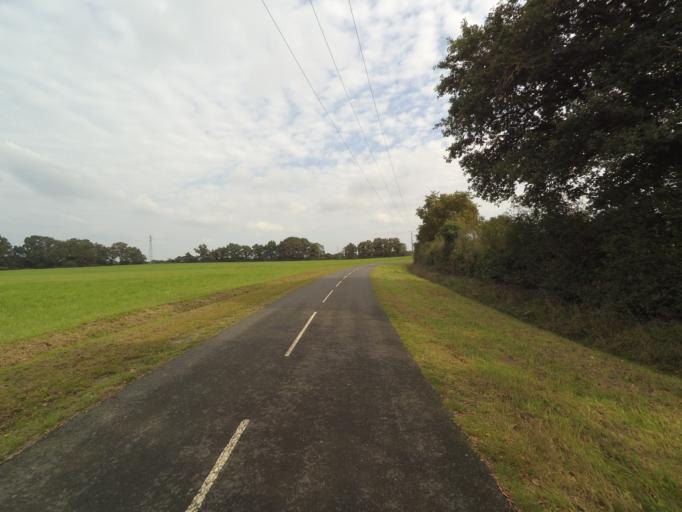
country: FR
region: Pays de la Loire
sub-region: Departement de la Vendee
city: Bouffere
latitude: 46.9749
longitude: -1.3492
